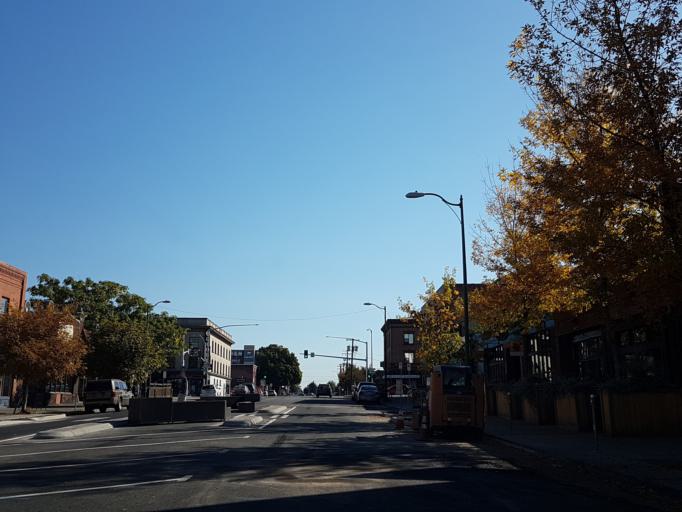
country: US
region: Washington
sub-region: Spokane County
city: Spokane
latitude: 47.6590
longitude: -117.4126
